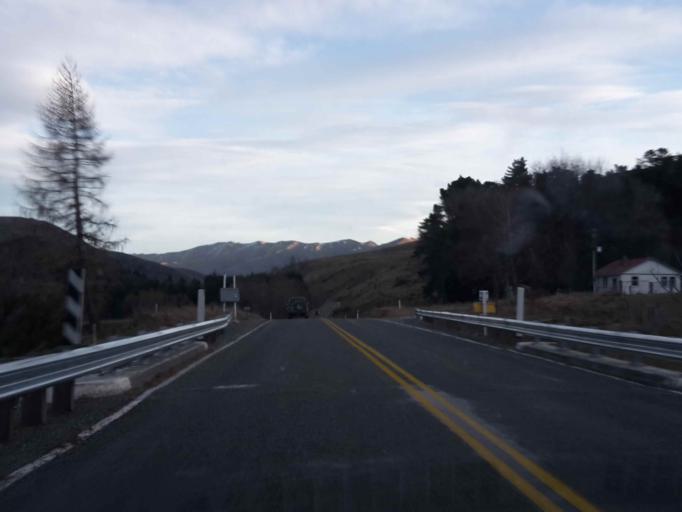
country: NZ
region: Canterbury
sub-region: Timaru District
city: Pleasant Point
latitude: -44.0499
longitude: 170.6804
